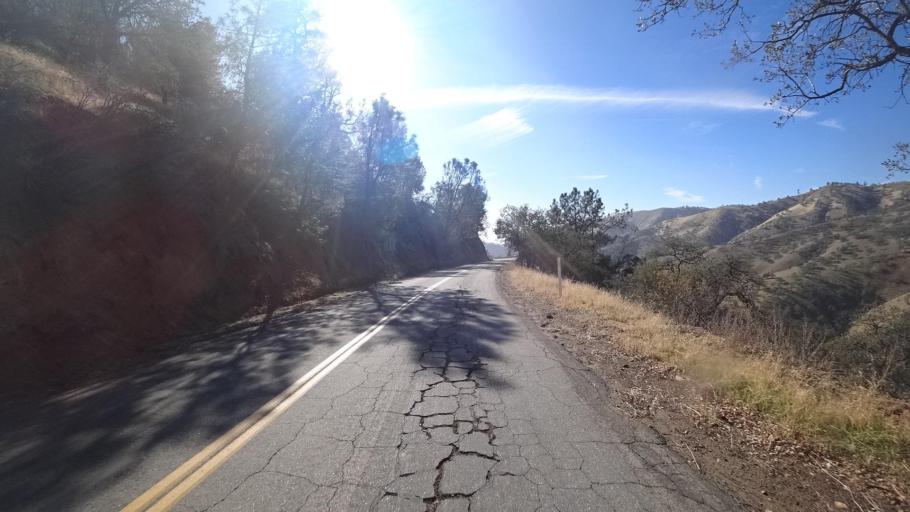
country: US
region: California
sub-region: Kern County
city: Bear Valley Springs
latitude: 35.3361
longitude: -118.5829
